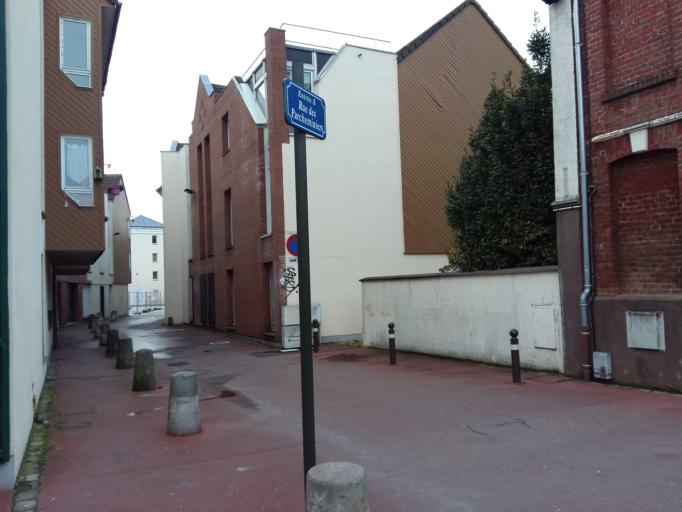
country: FR
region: Picardie
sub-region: Departement de la Somme
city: Amiens
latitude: 49.9006
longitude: 2.3024
